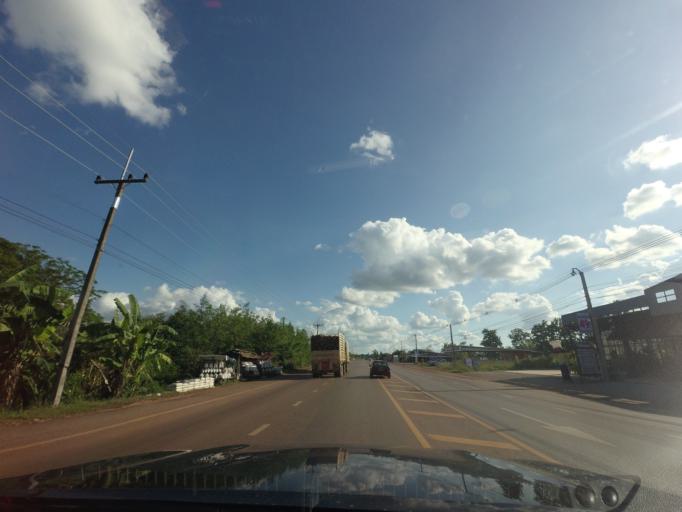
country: TH
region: Changwat Udon Thani
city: Ban Dung
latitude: 17.7280
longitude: 103.2516
